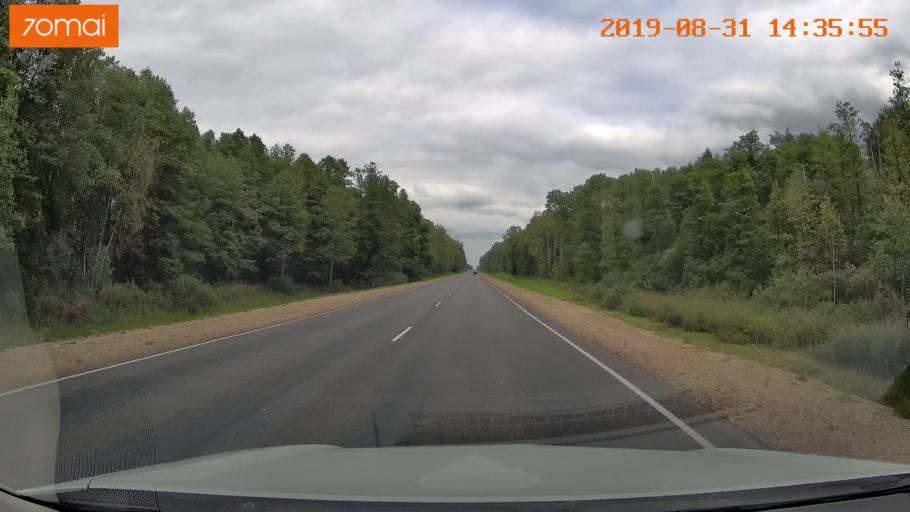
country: RU
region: Smolensk
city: Yekimovichi
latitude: 54.1662
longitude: 33.4671
